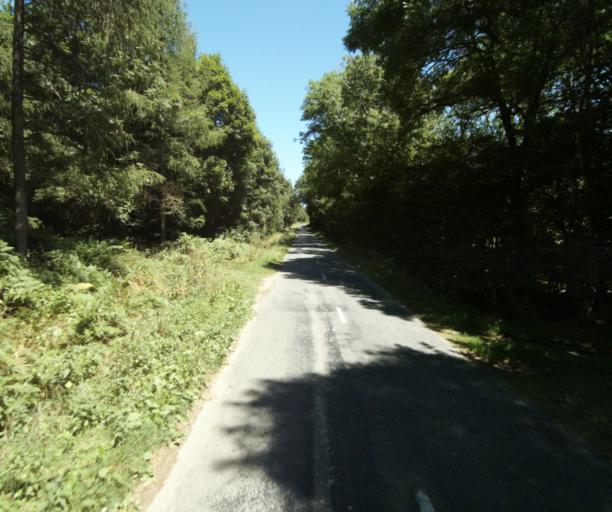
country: FR
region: Midi-Pyrenees
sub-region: Departement du Tarn
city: Dourgne
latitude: 43.4447
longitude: 2.1861
